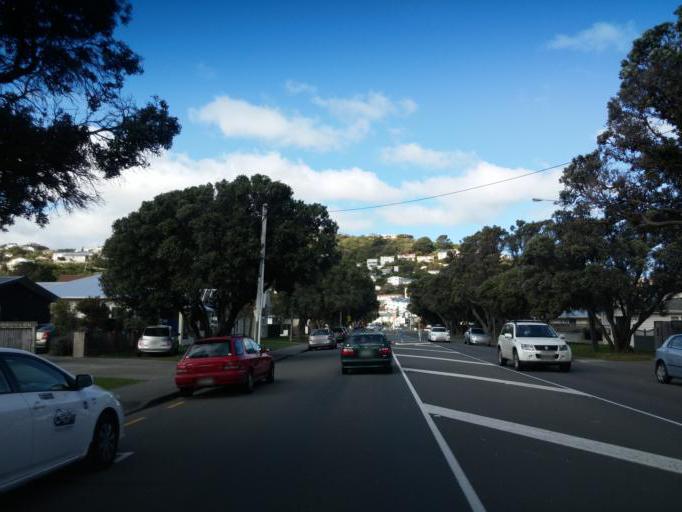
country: NZ
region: Wellington
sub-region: Wellington City
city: Wellington
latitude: -41.3168
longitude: 174.8174
